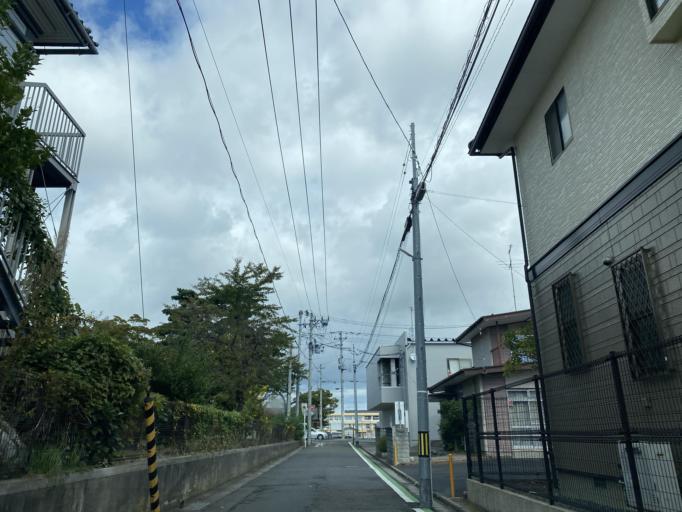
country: JP
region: Fukushima
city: Koriyama
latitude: 37.3917
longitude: 140.3511
